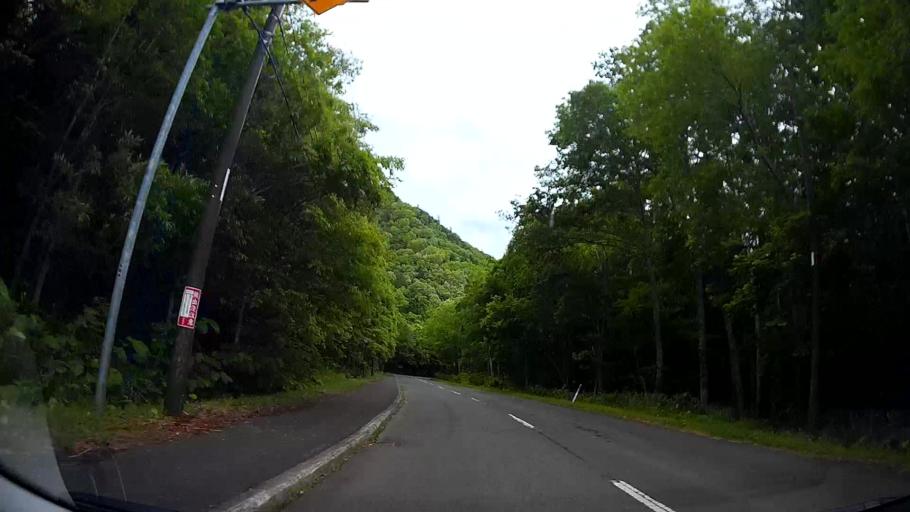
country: JP
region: Hokkaido
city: Sapporo
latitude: 42.9331
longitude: 141.1590
